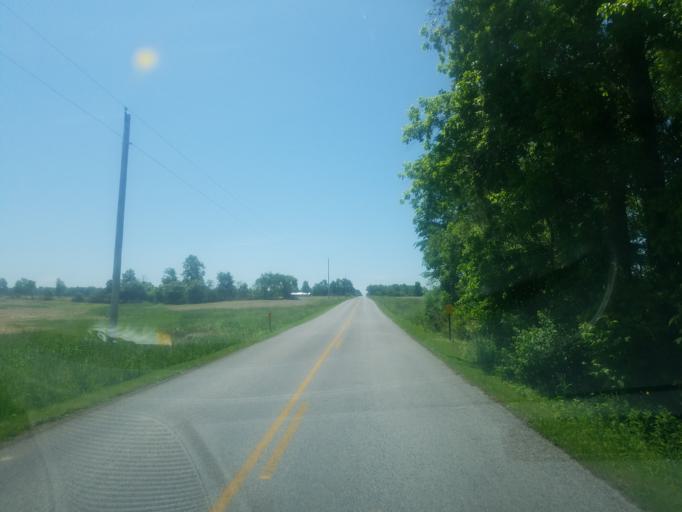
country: US
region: Ohio
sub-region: Huron County
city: New London
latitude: 41.1563
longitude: -82.3797
